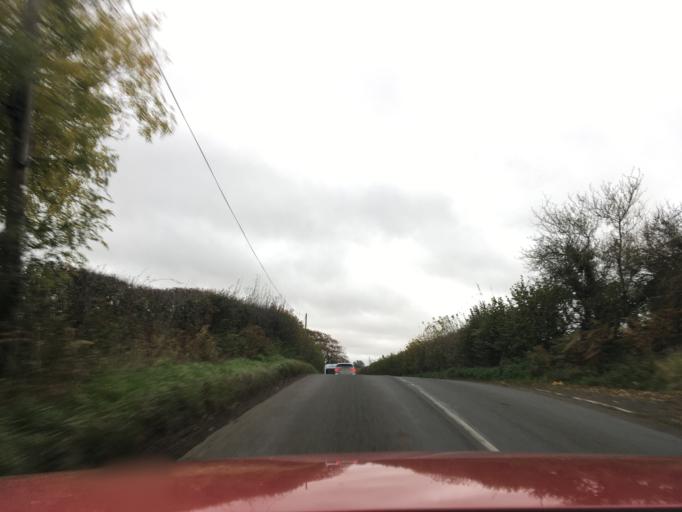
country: GB
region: England
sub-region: Dorset
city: Sherborne
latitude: 50.9805
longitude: -2.5646
